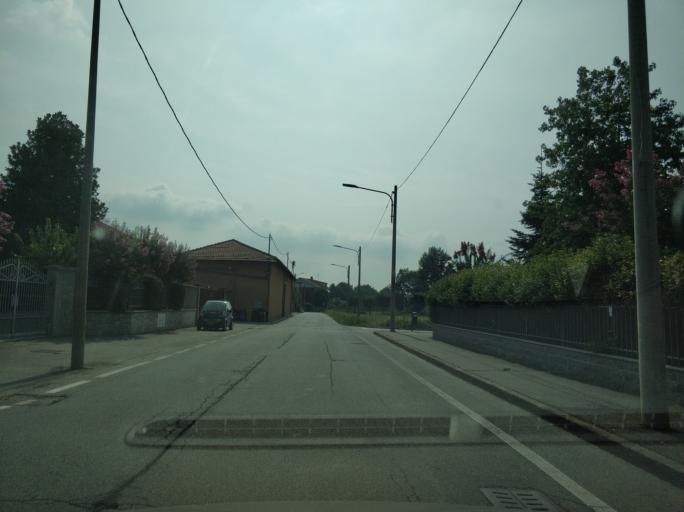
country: IT
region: Piedmont
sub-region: Provincia di Torino
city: San Maurizio
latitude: 45.1998
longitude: 7.6174
